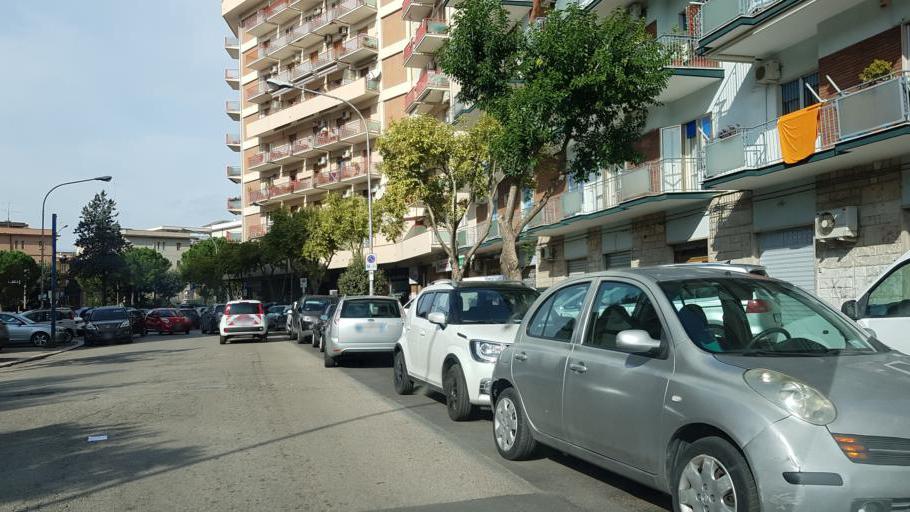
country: IT
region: Apulia
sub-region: Provincia di Foggia
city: Foggia
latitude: 41.4546
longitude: 15.5601
